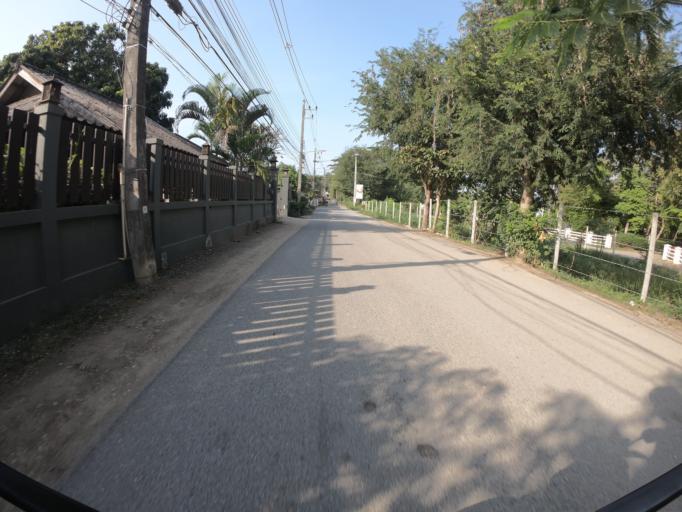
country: TH
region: Chiang Mai
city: Chiang Mai
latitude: 18.8481
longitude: 98.9837
